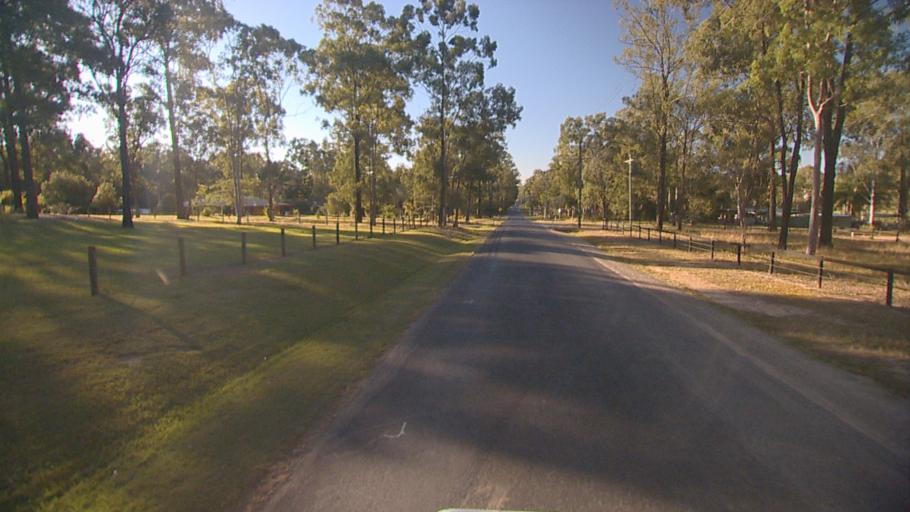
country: AU
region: Queensland
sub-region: Logan
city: Chambers Flat
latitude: -27.7655
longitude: 153.1385
